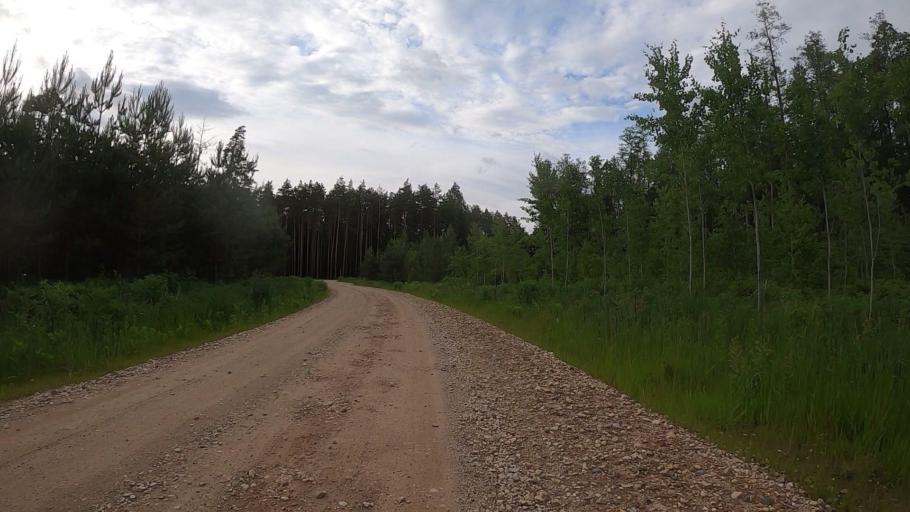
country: LV
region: Olaine
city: Olaine
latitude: 56.7696
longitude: 23.9037
